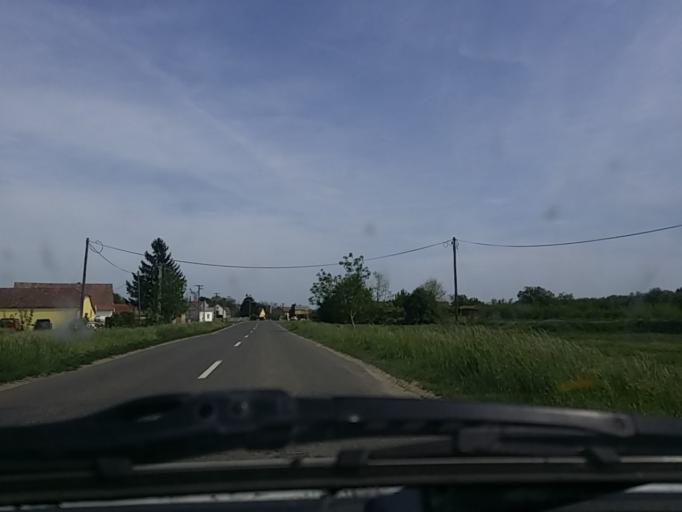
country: HU
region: Baranya
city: Harkany
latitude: 45.8388
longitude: 18.1583
